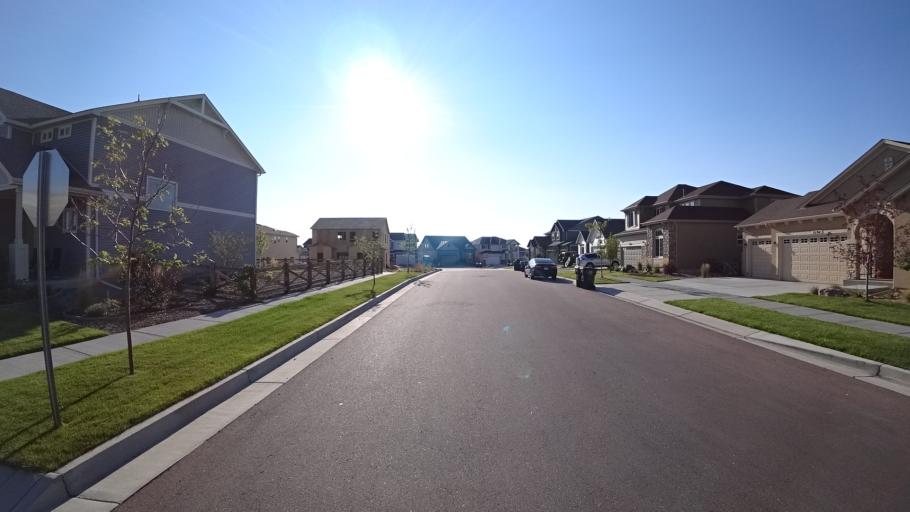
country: US
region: Colorado
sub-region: El Paso County
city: Cimarron Hills
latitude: 38.9335
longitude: -104.6583
